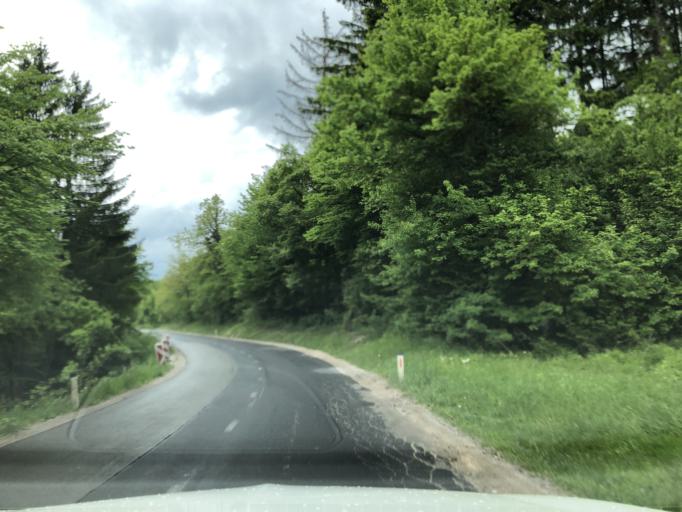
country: SI
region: Bloke
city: Nova Vas
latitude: 45.7625
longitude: 14.4468
